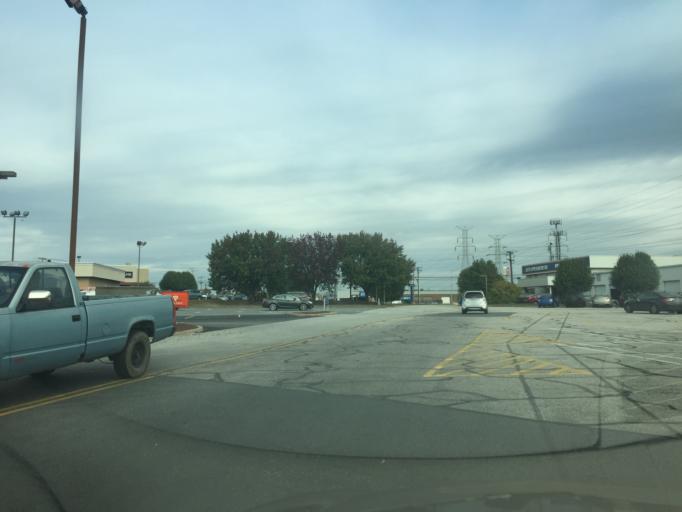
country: US
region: Maryland
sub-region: Baltimore County
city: Dundalk
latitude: 39.2790
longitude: -76.5038
